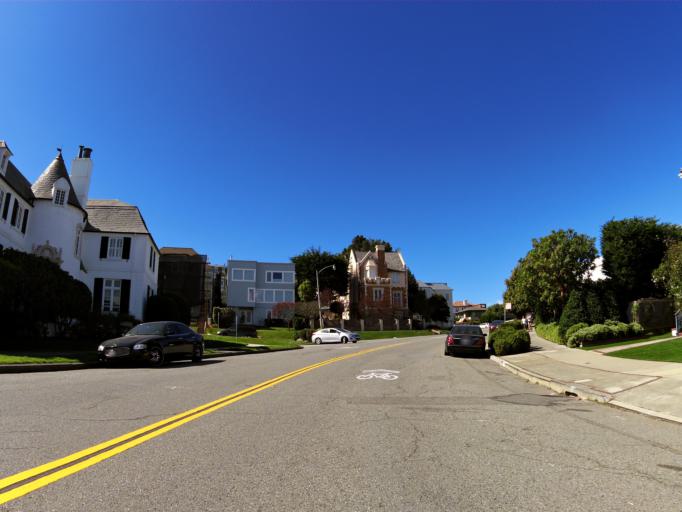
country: US
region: California
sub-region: San Francisco County
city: San Francisco
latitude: 37.7862
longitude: -122.4913
